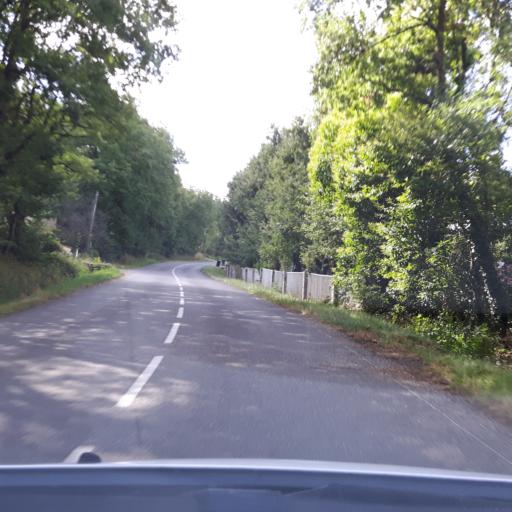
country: FR
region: Midi-Pyrenees
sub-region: Departement de la Haute-Garonne
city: Bouloc
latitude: 43.7957
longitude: 1.4131
